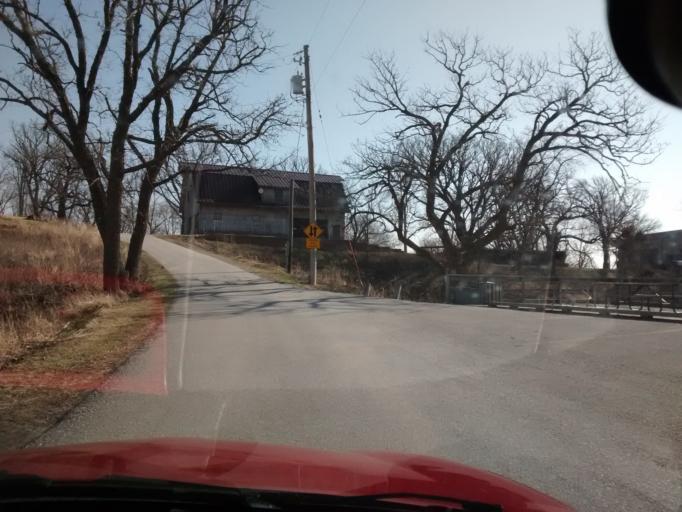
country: US
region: Iowa
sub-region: Pottawattamie County
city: Carter Lake
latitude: 41.4141
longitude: -95.8562
